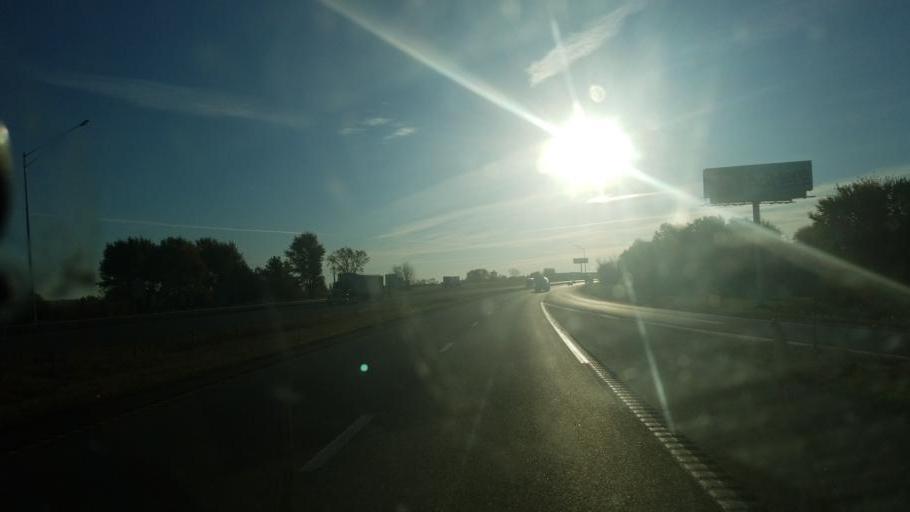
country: US
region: Missouri
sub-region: Warren County
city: Warrenton
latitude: 38.8574
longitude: -91.3020
